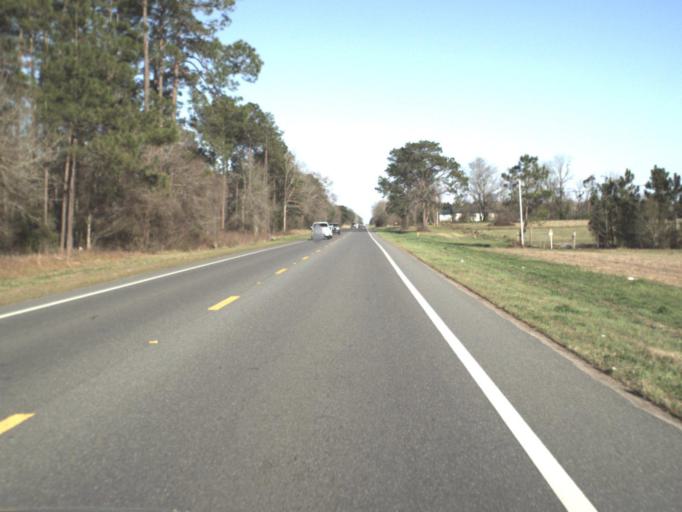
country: US
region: Florida
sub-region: Jackson County
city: Sneads
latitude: 30.7197
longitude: -85.0609
